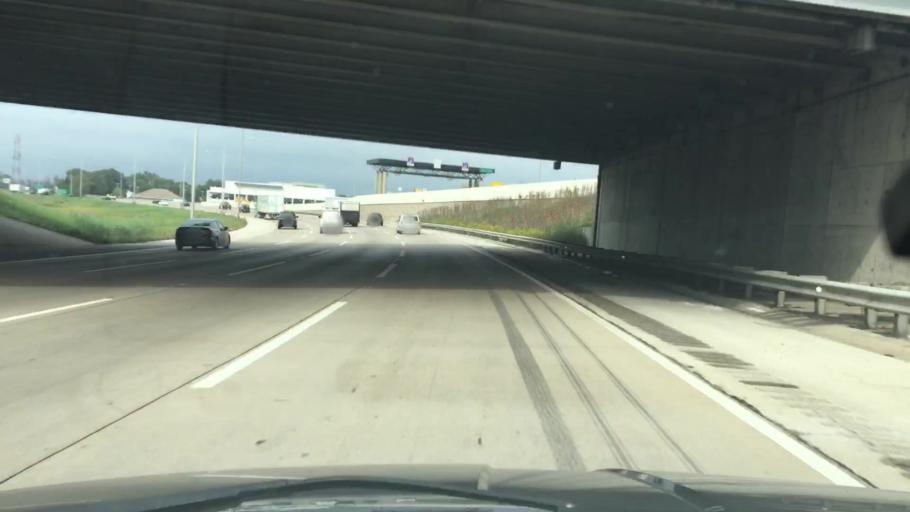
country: US
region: Illinois
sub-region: Lake County
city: Riverwoods
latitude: 42.1528
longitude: -87.8721
